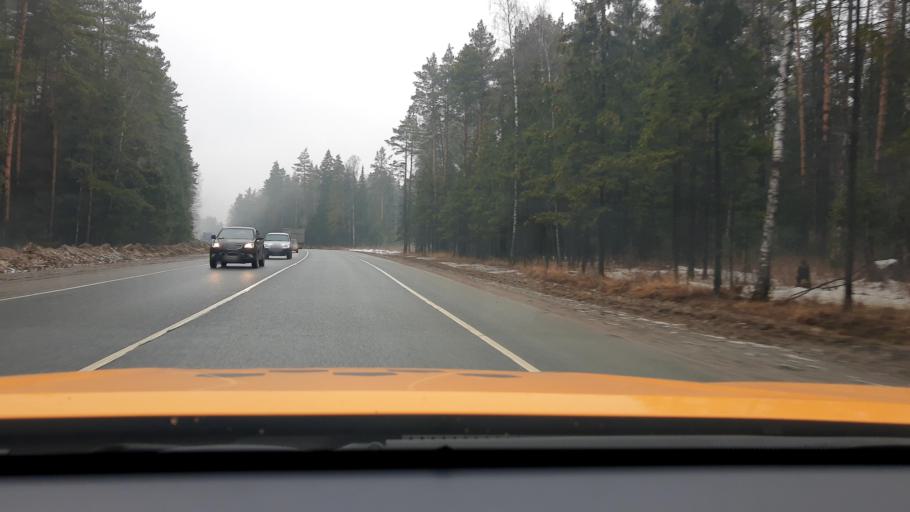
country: RU
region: Moskovskaya
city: Yamkino
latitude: 55.9482
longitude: 38.3926
